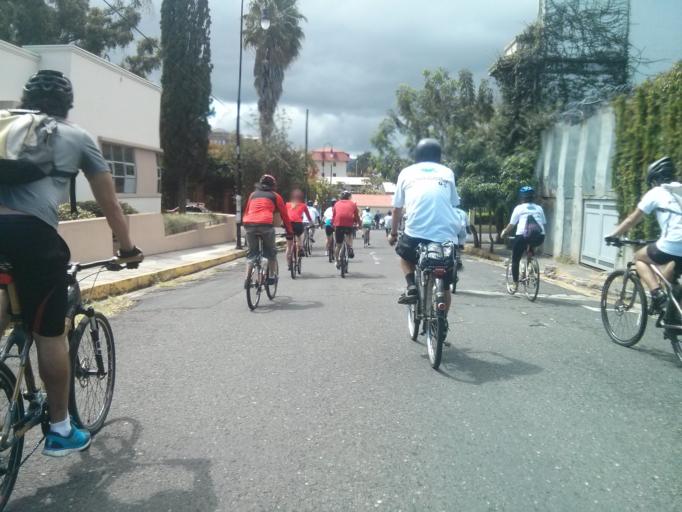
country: CR
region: San Jose
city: San Jose
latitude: 9.9376
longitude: -84.0724
